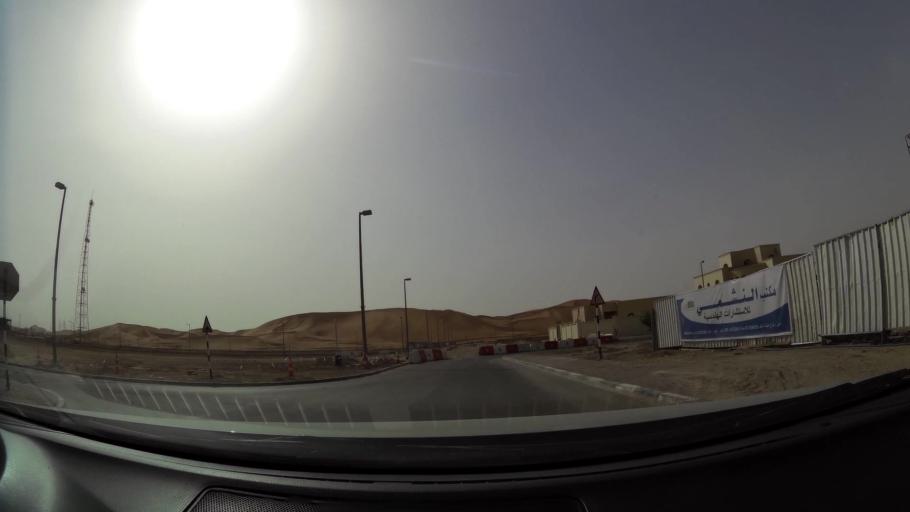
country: AE
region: Abu Dhabi
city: Al Ain
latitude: 24.2112
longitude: 55.5807
